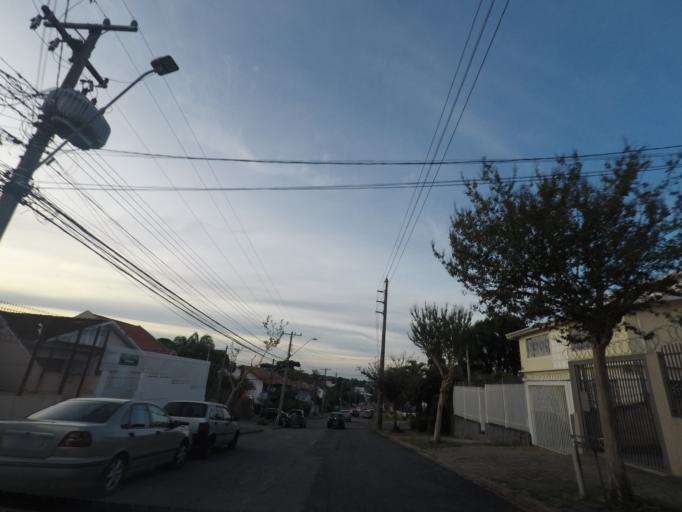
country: BR
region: Parana
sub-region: Curitiba
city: Curitiba
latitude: -25.4203
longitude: -49.2844
